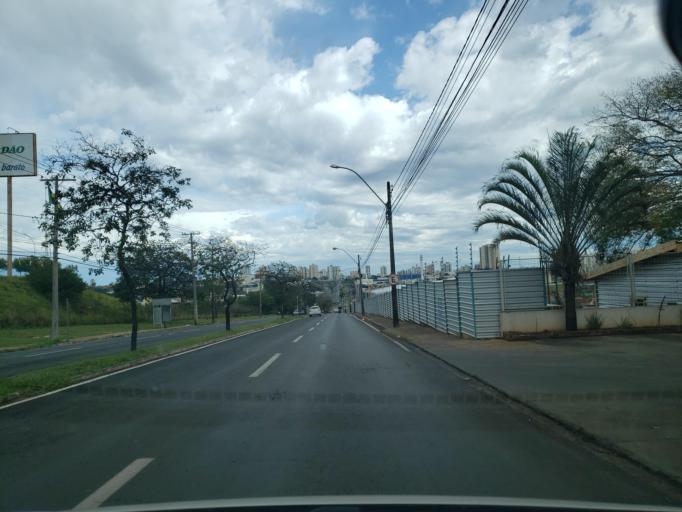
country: BR
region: Sao Paulo
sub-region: Bauru
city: Bauru
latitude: -22.3356
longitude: -49.0331
